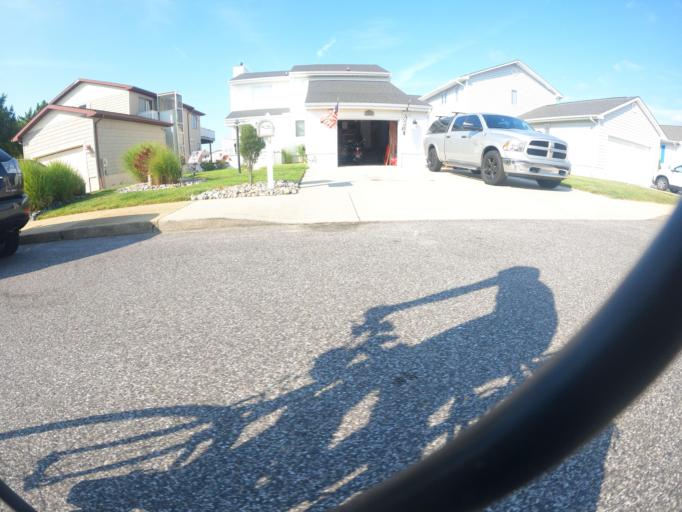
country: US
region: Delaware
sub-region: Sussex County
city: Bethany Beach
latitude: 38.4440
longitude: -75.0645
